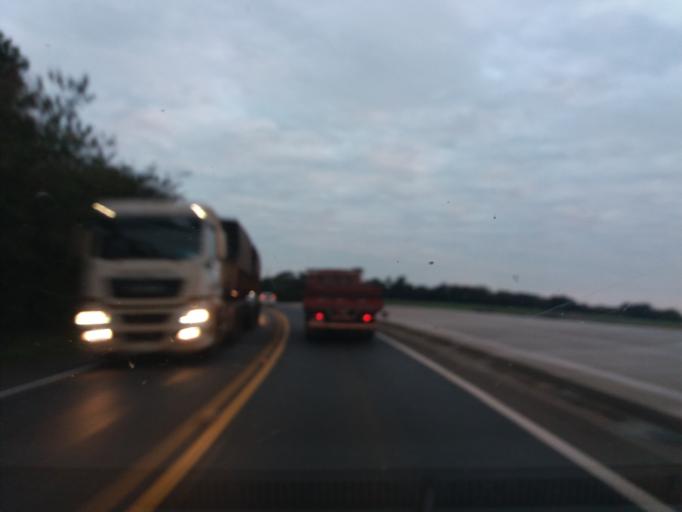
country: BR
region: Parana
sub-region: Realeza
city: Realeza
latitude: -25.3884
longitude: -53.5775
